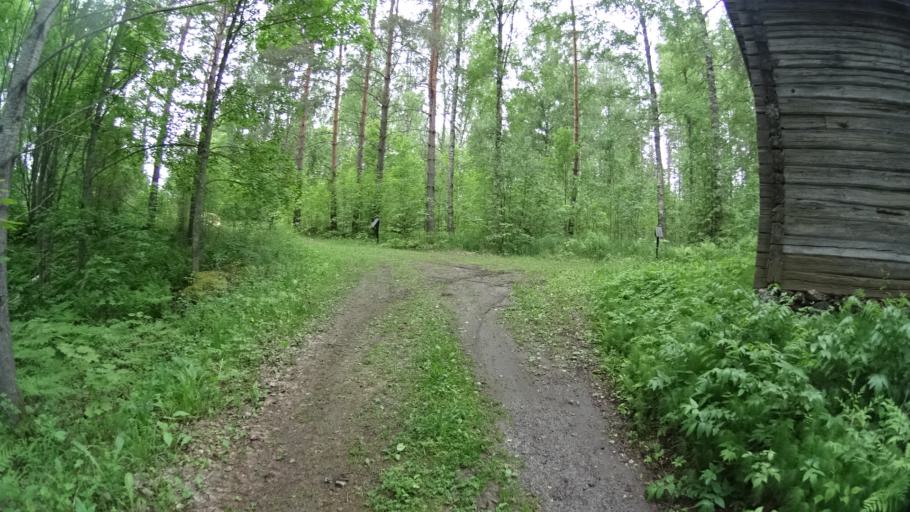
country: FI
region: Southern Savonia
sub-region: Savonlinna
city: Savonlinna
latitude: 61.9218
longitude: 28.8264
